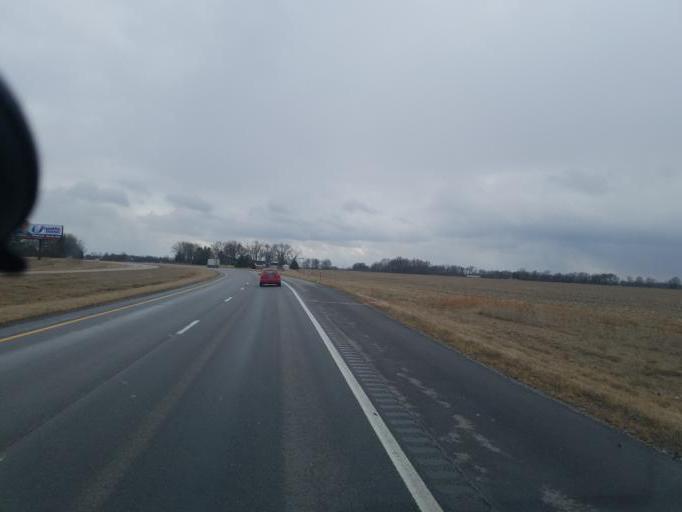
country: US
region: Missouri
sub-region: Randolph County
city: Moberly
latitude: 39.3799
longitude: -92.4136
